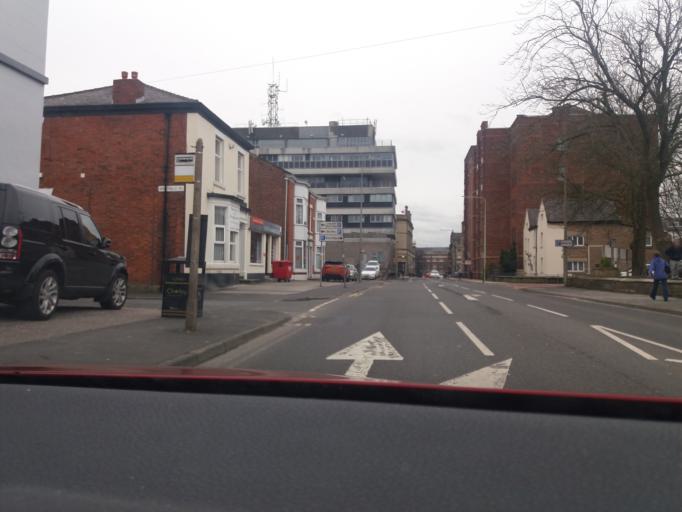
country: GB
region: England
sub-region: Lancashire
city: Chorley
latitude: 53.6536
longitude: -2.6358
